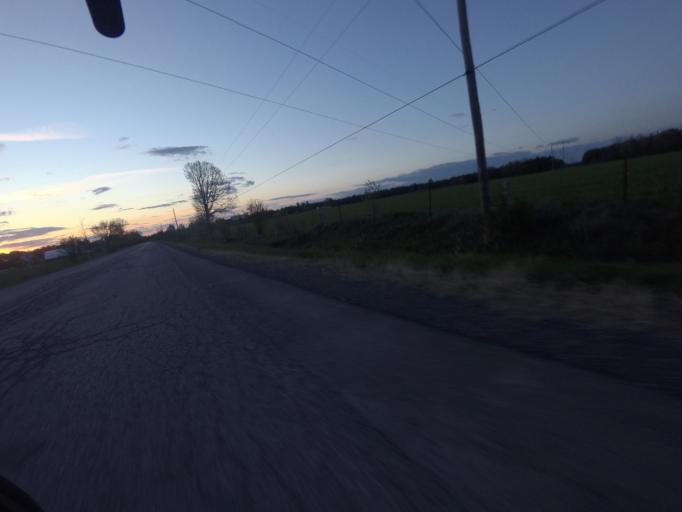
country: CA
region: Ontario
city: Arnprior
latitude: 45.4292
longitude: -76.2373
